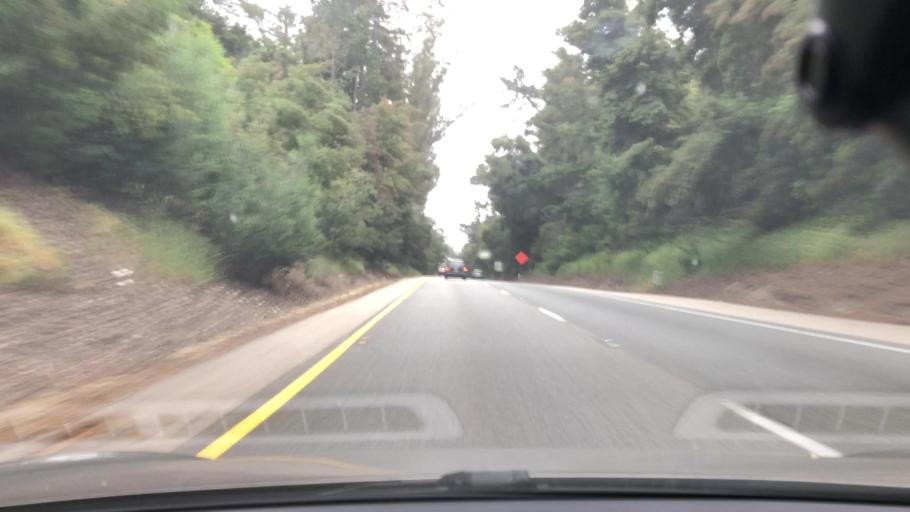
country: US
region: California
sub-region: Santa Cruz County
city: Pasatiempo
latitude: 37.0168
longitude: -122.0273
